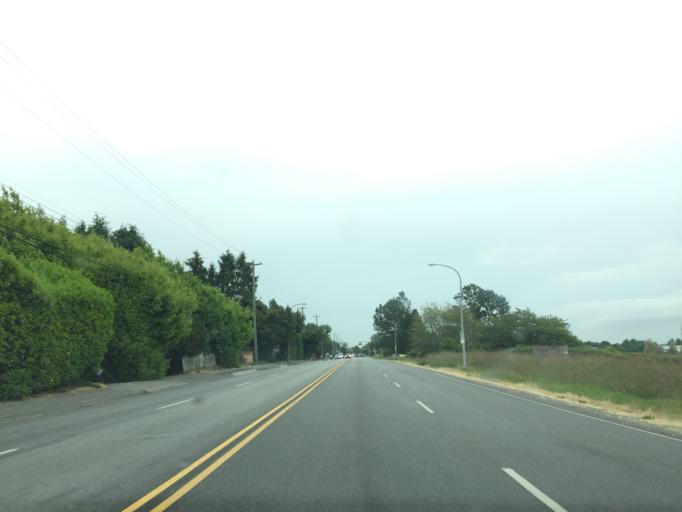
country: CA
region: British Columbia
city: Richmond
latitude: 49.1334
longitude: -123.1107
